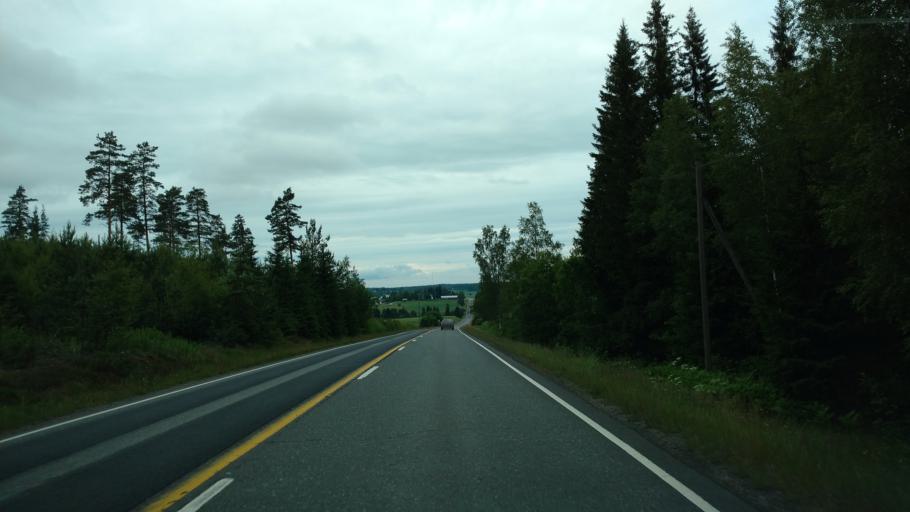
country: FI
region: Varsinais-Suomi
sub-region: Salo
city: Halikko
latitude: 60.4640
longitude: 23.0185
